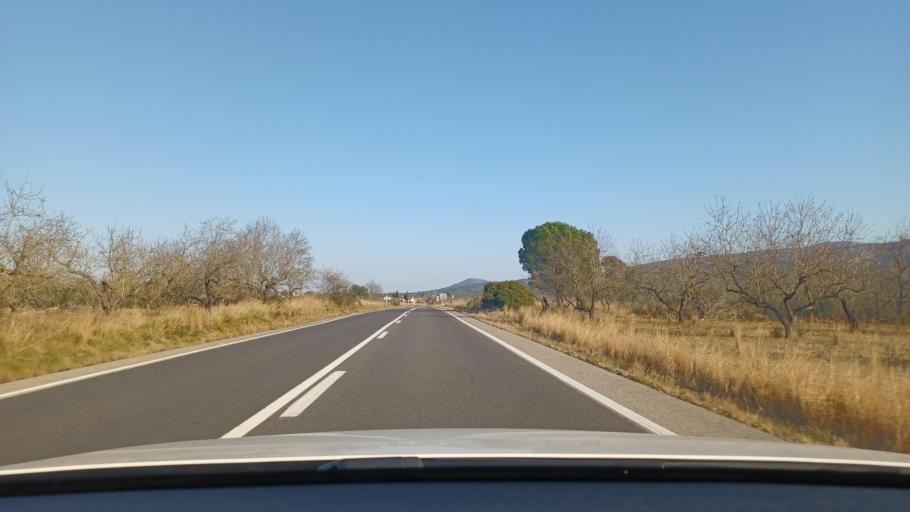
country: ES
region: Catalonia
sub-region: Provincia de Tarragona
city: Santa Barbara
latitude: 40.6776
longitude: 0.4515
